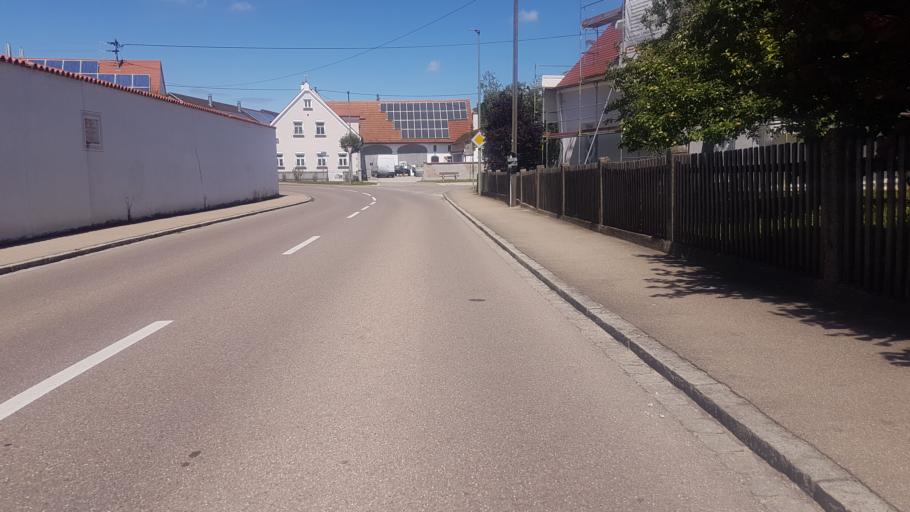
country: DE
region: Bavaria
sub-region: Swabia
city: Blindheim
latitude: 48.6313
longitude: 10.6184
